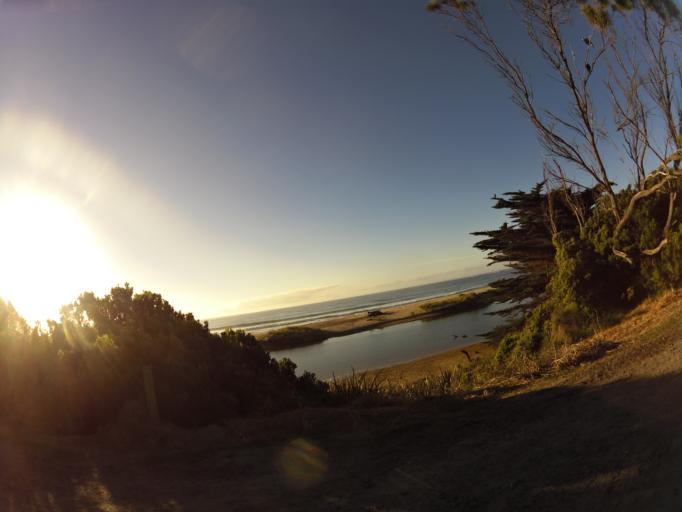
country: AU
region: Victoria
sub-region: Colac-Otway
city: Apollo Bay
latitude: -38.7621
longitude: 143.6740
